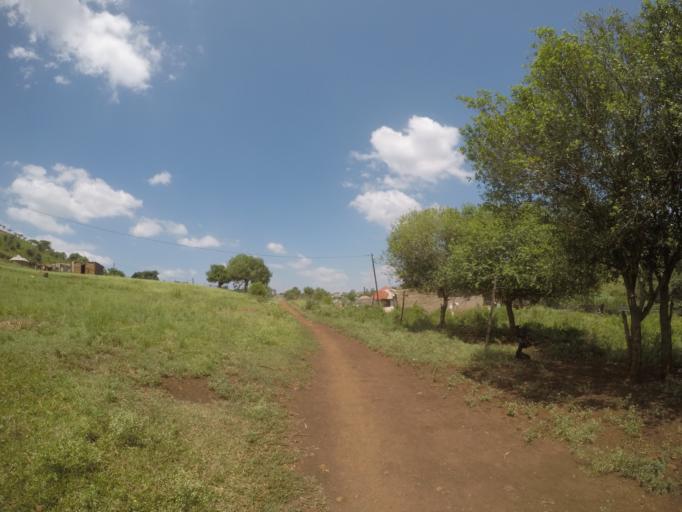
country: ZA
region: KwaZulu-Natal
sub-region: uThungulu District Municipality
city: Empangeni
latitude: -28.5993
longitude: 31.7377
